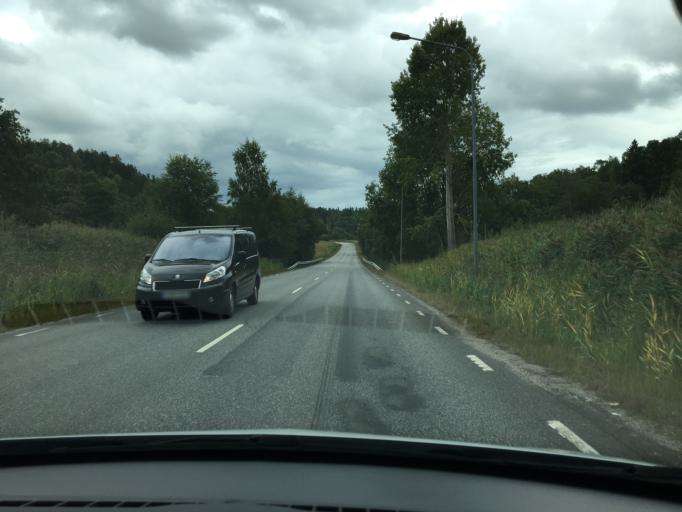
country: SE
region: Vaestra Goetaland
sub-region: Ale Kommun
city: Alafors
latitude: 57.9221
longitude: 12.0830
